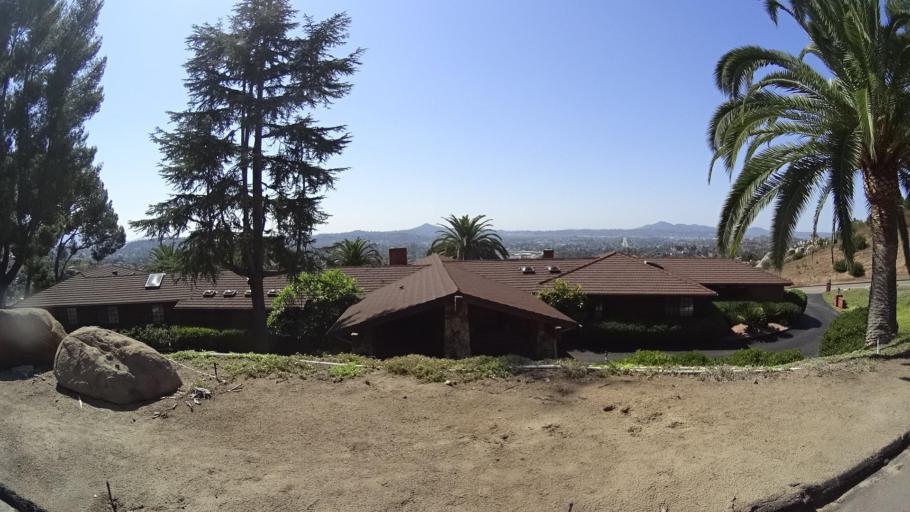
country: US
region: California
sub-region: San Diego County
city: Granite Hills
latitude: 32.8032
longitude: -116.8952
